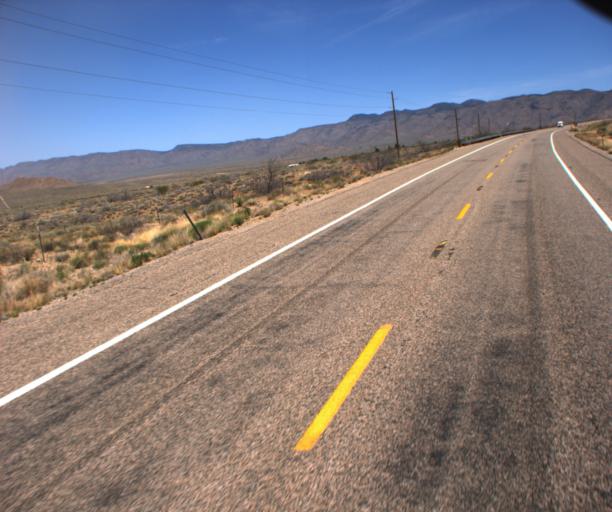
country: US
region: Arizona
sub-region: Mohave County
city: New Kingman-Butler
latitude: 35.4135
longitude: -113.8222
